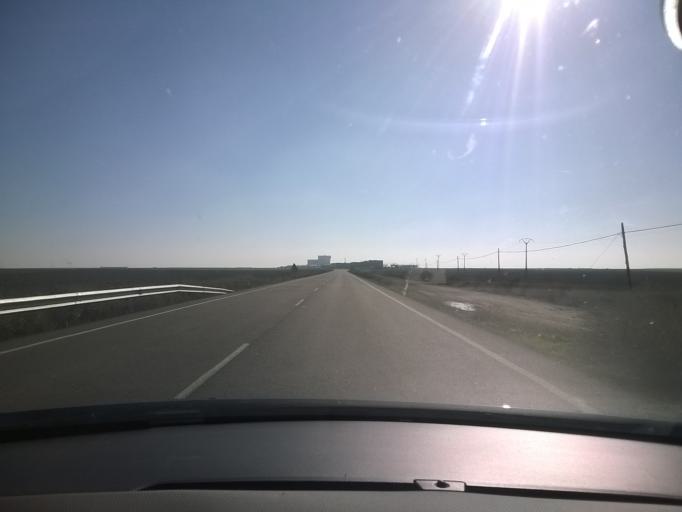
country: ES
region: Aragon
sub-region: Provincia de Zaragoza
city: Bujaraloz
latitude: 41.4908
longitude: -0.1514
